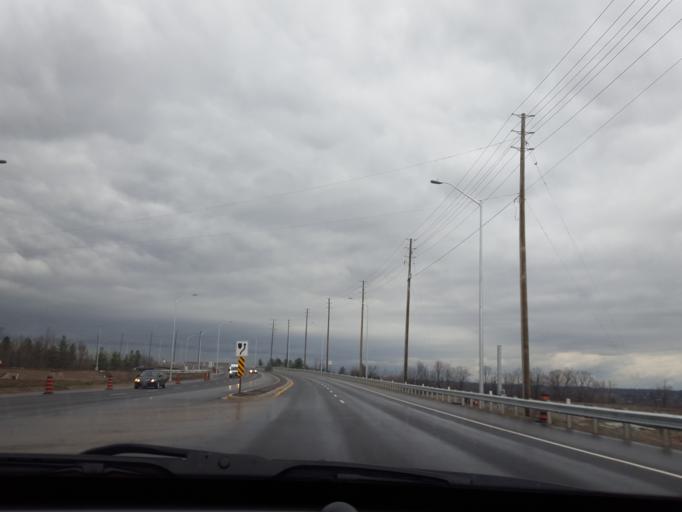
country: CA
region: Ontario
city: Pickering
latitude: 43.9118
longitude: -79.0954
